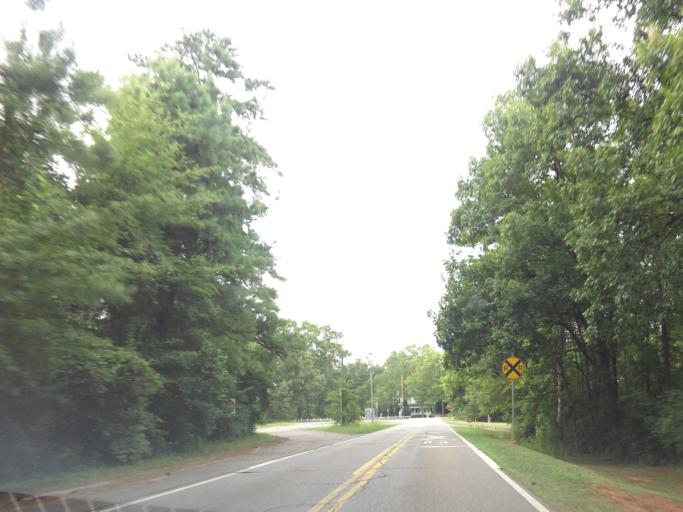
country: US
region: Georgia
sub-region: Bibb County
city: West Point
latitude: 32.9127
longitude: -83.7743
